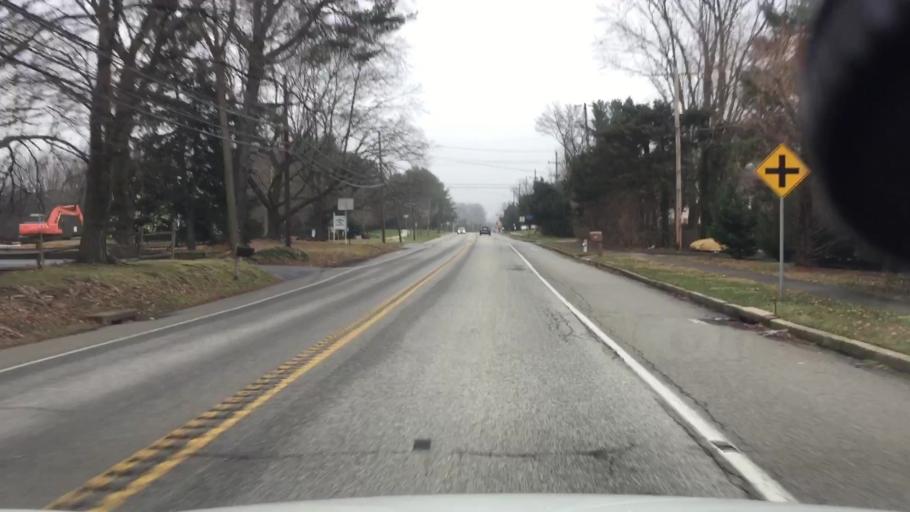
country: US
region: Pennsylvania
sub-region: Montgomery County
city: Dresher
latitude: 40.1531
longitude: -75.1871
